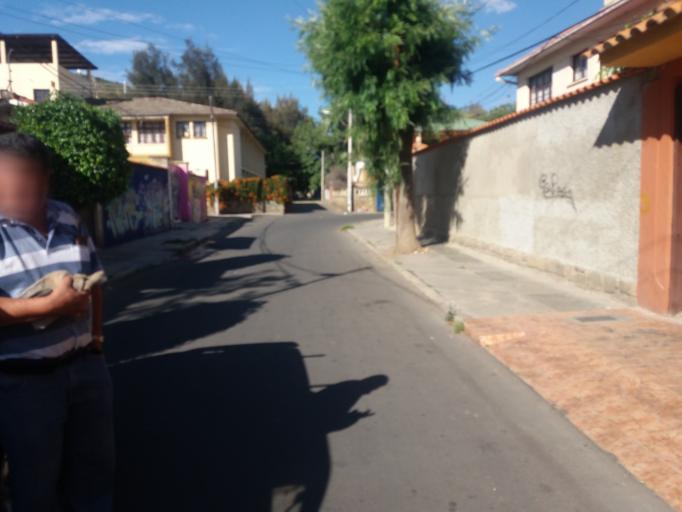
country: BO
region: Cochabamba
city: Cochabamba
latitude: -17.3910
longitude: -66.1465
